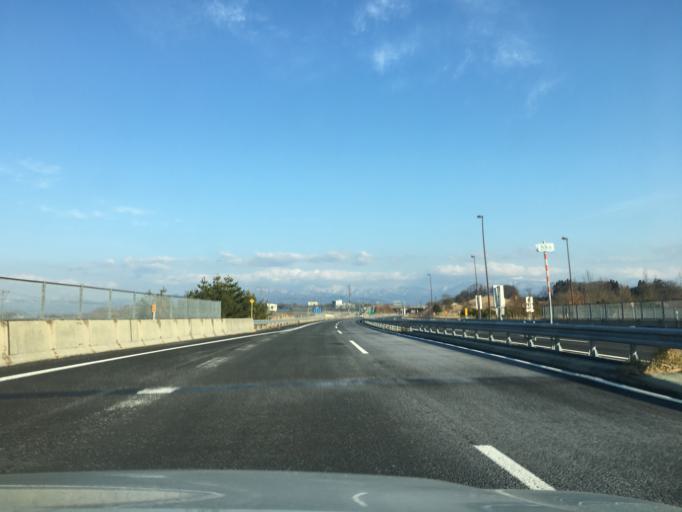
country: JP
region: Yamagata
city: Sagae
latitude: 38.3664
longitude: 140.2619
